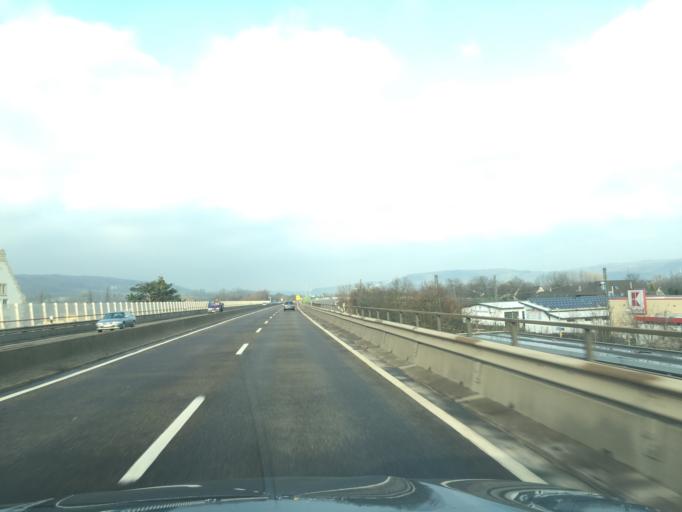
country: DE
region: Rheinland-Pfalz
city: Sinzig
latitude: 50.5467
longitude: 7.2577
